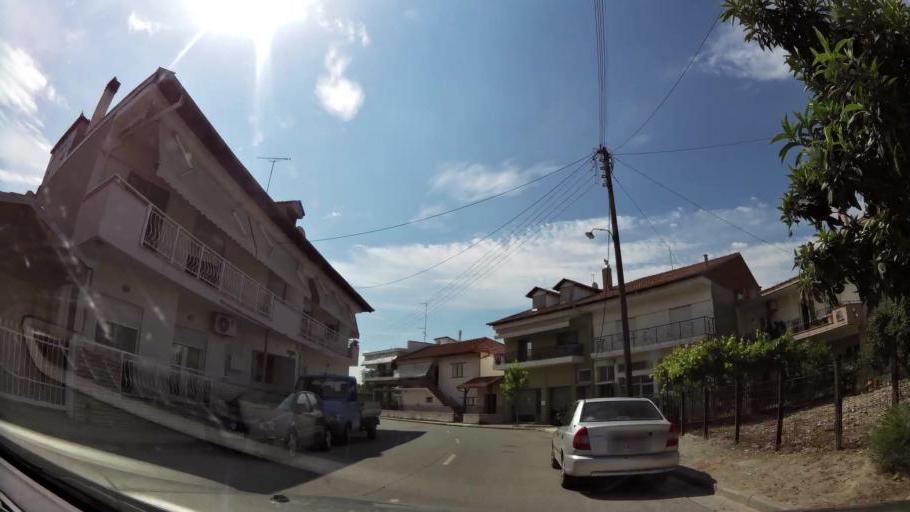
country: GR
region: Central Macedonia
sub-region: Nomos Pierias
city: Katerini
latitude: 40.2693
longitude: 22.4899
